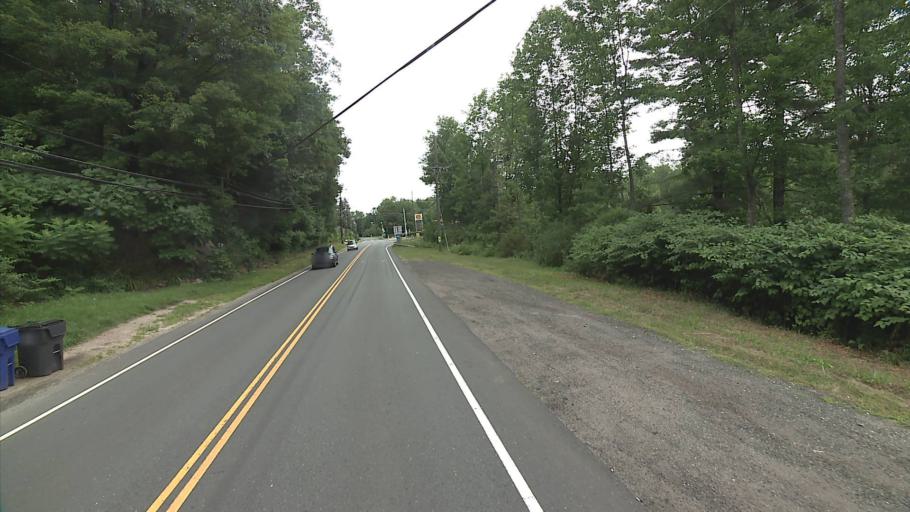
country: US
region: Connecticut
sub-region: Litchfield County
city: Winsted
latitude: 41.9453
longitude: -73.0516
